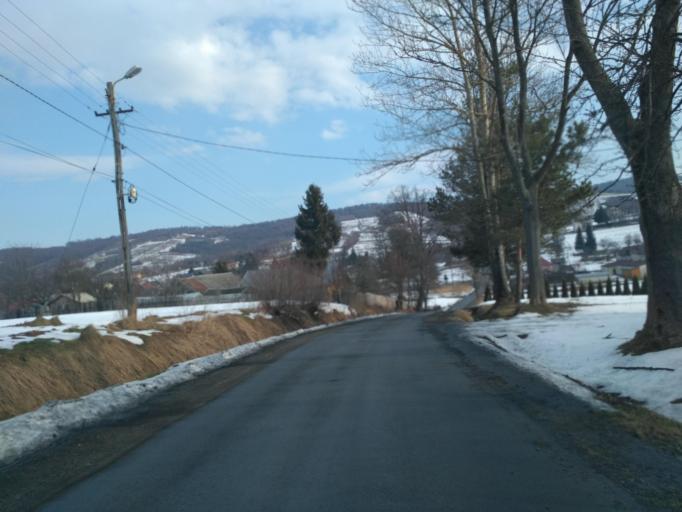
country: PL
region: Subcarpathian Voivodeship
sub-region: Powiat brzozowski
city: Niebocko
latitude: 49.6530
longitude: 22.1355
